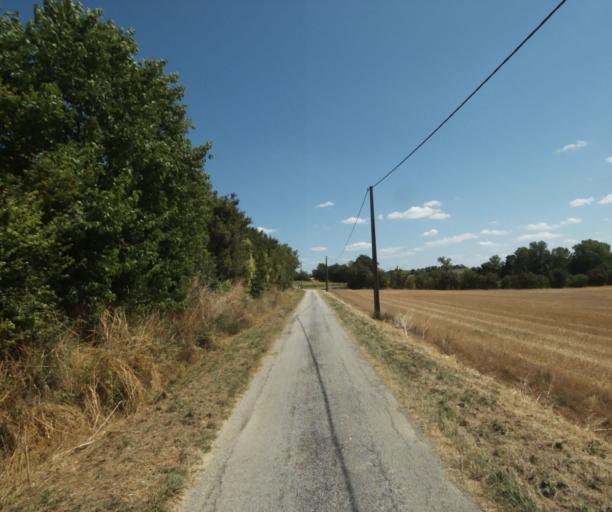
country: FR
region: Midi-Pyrenees
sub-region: Departement de la Haute-Garonne
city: Saint-Felix-Lauragais
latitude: 43.4852
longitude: 1.8977
